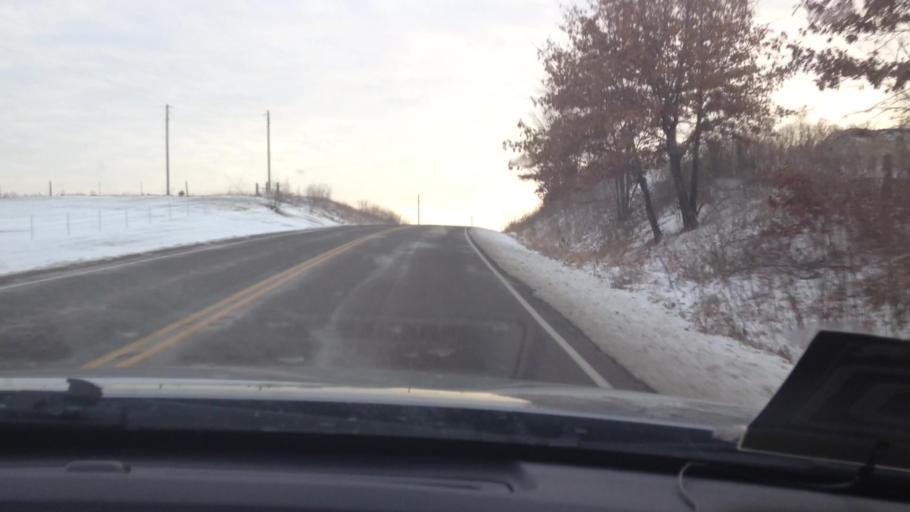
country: US
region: Kansas
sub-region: Leavenworth County
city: Leavenworth
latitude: 39.2581
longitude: -94.9725
